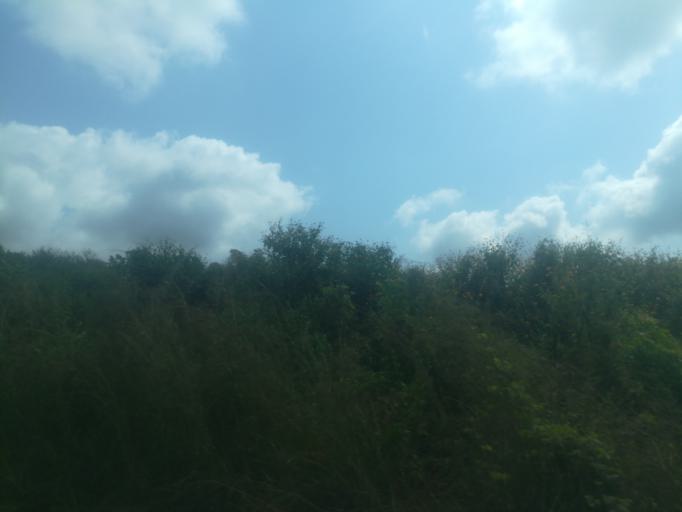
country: NG
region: Oyo
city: Moniya
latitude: 7.5807
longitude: 3.9152
